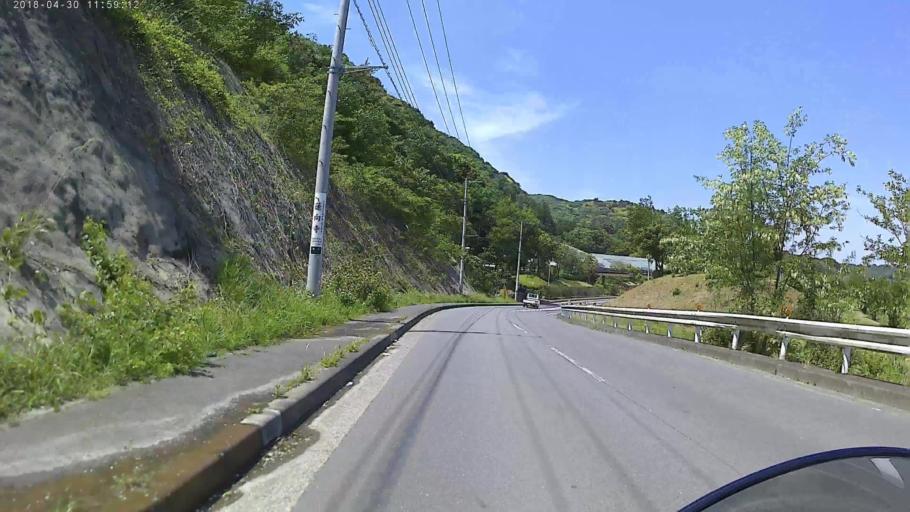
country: JP
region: Kanagawa
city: Zama
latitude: 35.5054
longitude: 139.3296
